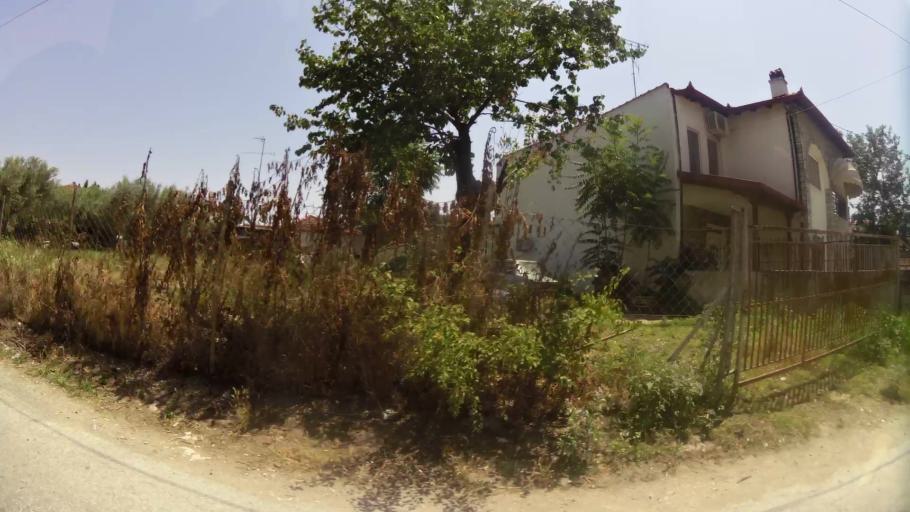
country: GR
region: Central Macedonia
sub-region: Nomos Thessalonikis
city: Epanomi
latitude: 40.4302
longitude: 22.9237
